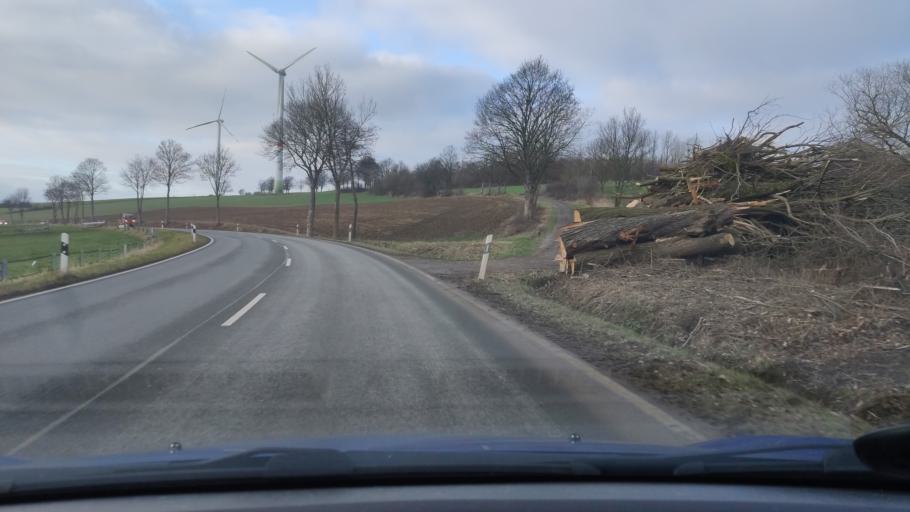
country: DE
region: Lower Saxony
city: Coppenbrugge
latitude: 52.1345
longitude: 9.5385
